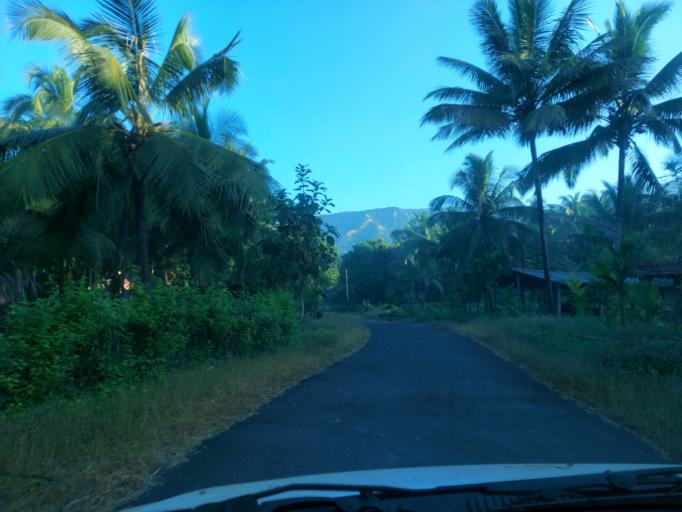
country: IN
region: Maharashtra
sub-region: Sindhudurg
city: Kudal
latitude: 16.0676
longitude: 73.8238
